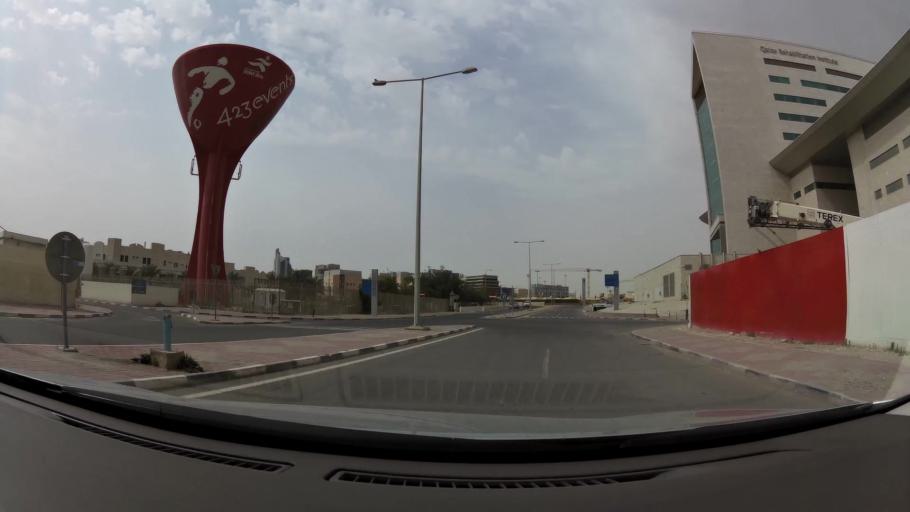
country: QA
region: Baladiyat ad Dawhah
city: Doha
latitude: 25.2943
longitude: 51.5104
